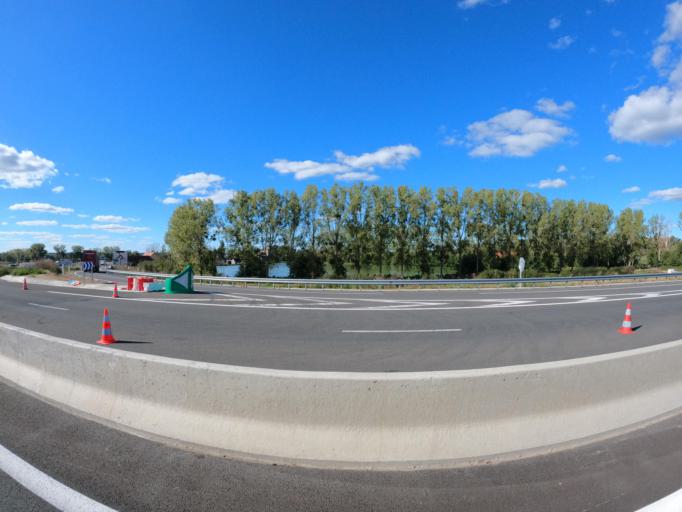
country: FR
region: Auvergne
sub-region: Departement de l'Allier
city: Toulon-sur-Allier
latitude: 46.4968
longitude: 3.3655
